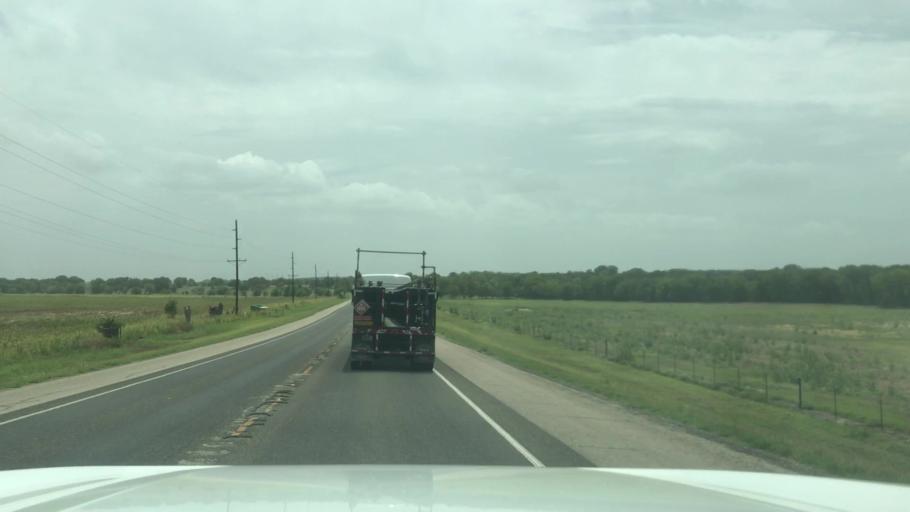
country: US
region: Texas
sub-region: Bosque County
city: Clifton
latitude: 31.7147
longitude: -97.5469
